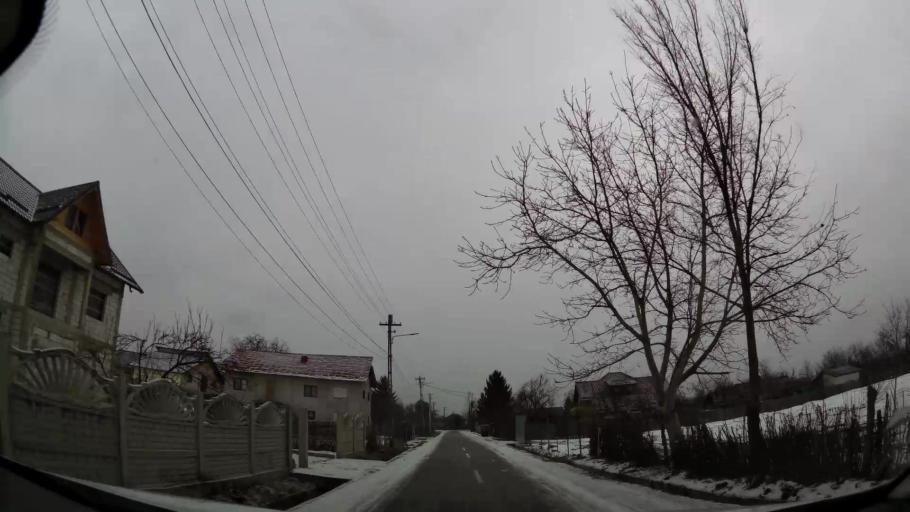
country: RO
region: Dambovita
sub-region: Comuna Aninoasa
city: Viforata
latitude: 44.9425
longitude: 25.4734
